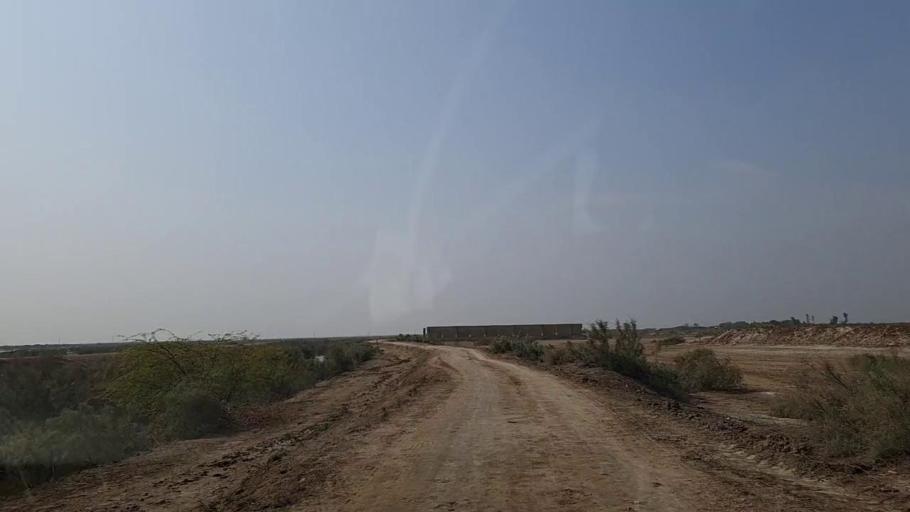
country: PK
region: Sindh
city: Gharo
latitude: 24.6737
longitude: 67.7128
